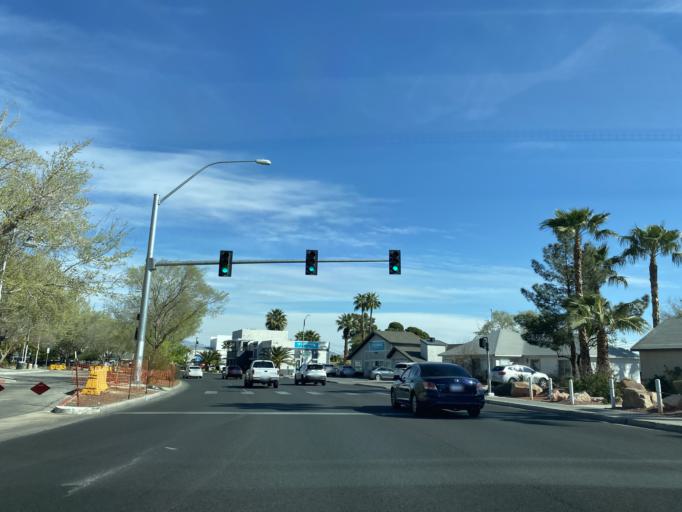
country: US
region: Nevada
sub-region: Clark County
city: Las Vegas
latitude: 36.1557
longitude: -115.1366
